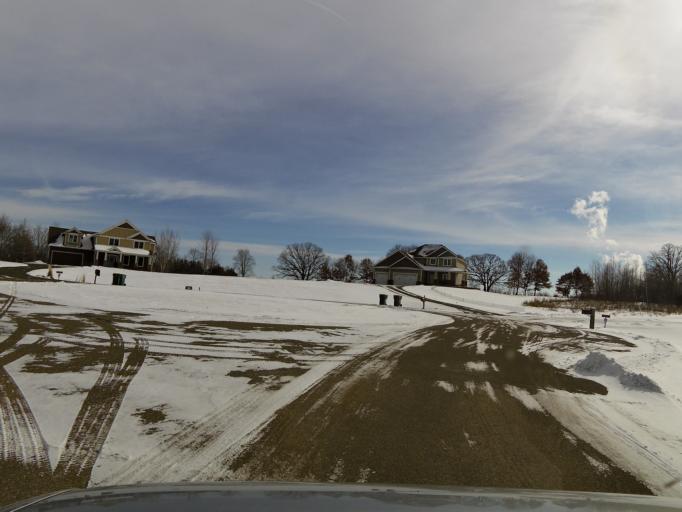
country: US
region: Minnesota
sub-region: Washington County
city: Stillwater
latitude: 45.0655
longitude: -92.7702
